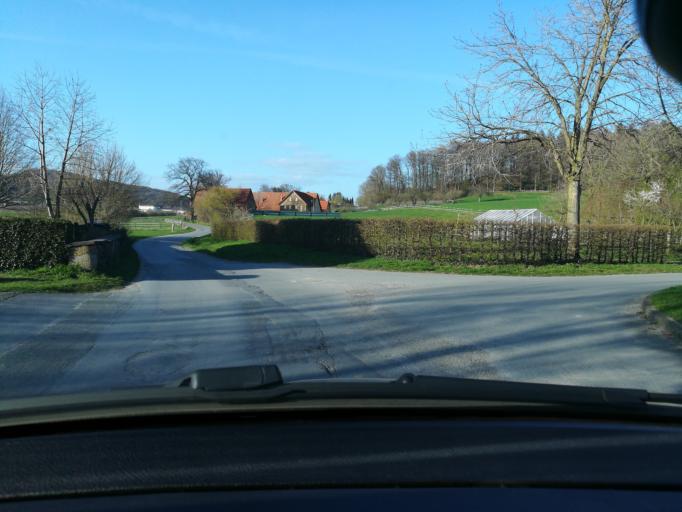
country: DE
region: North Rhine-Westphalia
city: Borgholzhausen
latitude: 52.0875
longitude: 8.2916
